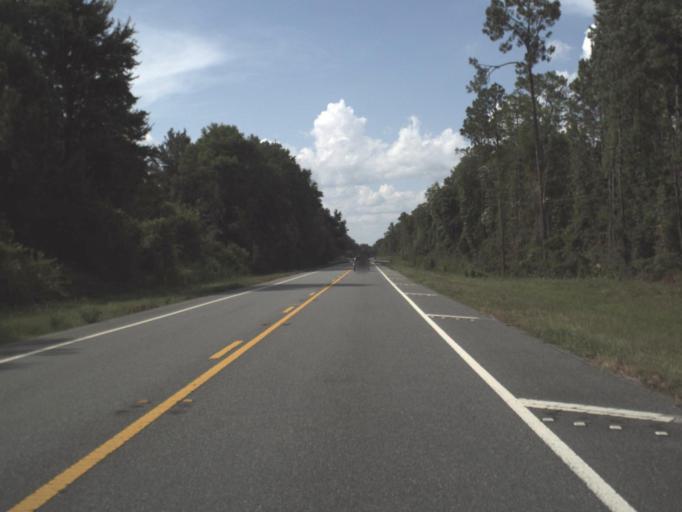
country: US
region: Florida
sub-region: Taylor County
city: Perry
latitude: 30.2664
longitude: -83.6267
